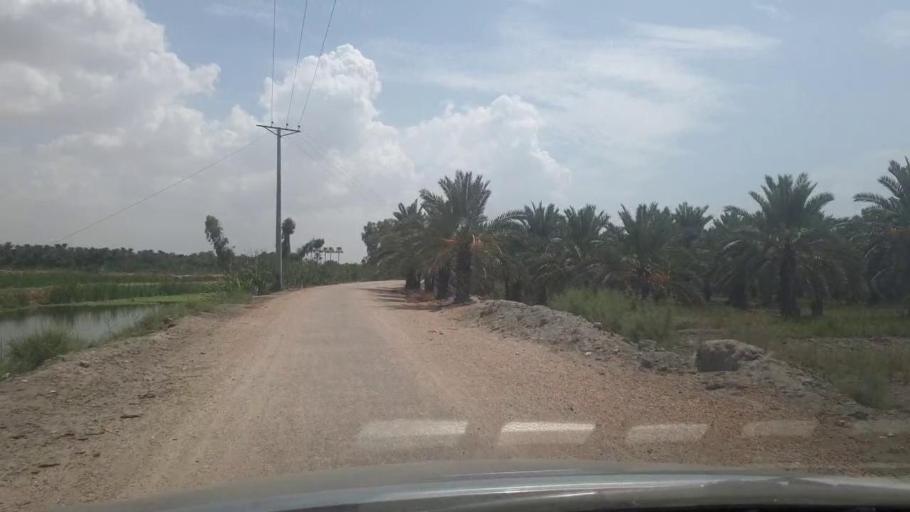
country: PK
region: Sindh
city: Khairpur
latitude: 27.4764
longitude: 68.8100
